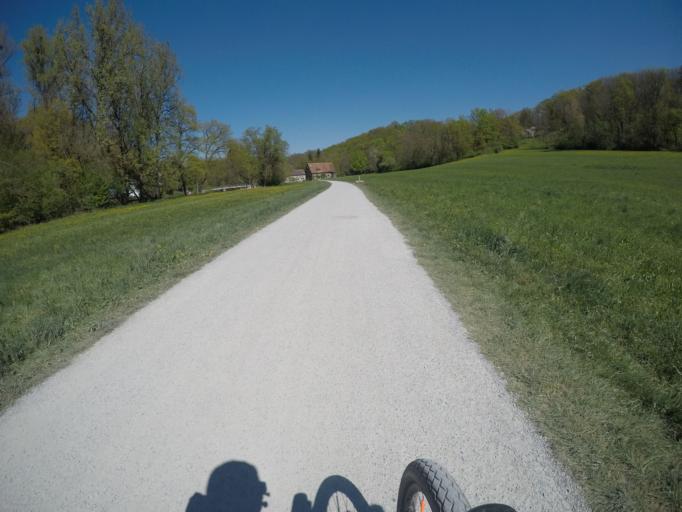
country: DE
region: Baden-Wuerttemberg
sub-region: Regierungsbezirk Stuttgart
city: Waiblingen
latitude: 48.8612
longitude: 9.3027
